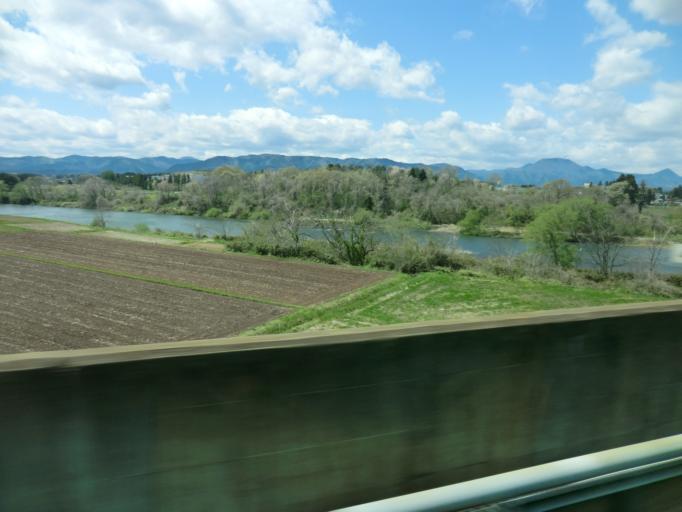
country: JP
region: Iwate
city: Hanamaki
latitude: 39.5076
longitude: 141.1733
